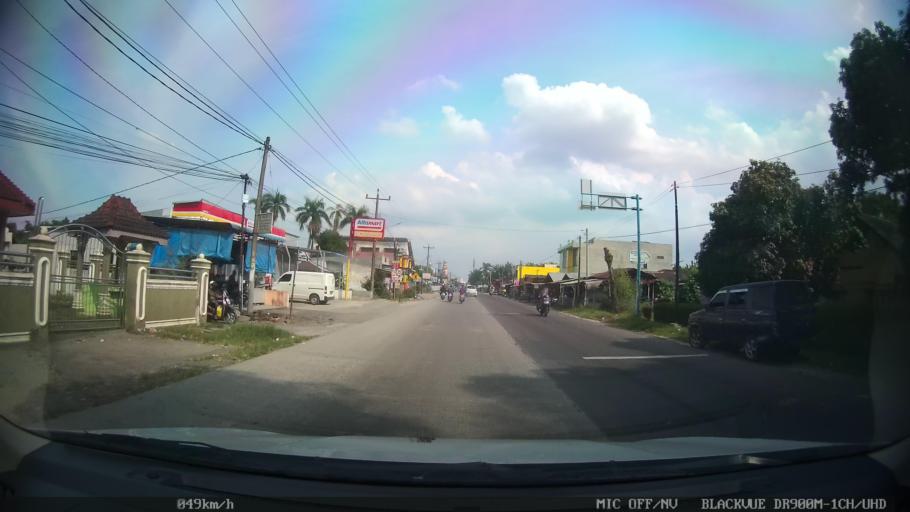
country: ID
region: North Sumatra
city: Binjai
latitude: 3.6298
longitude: 98.4924
